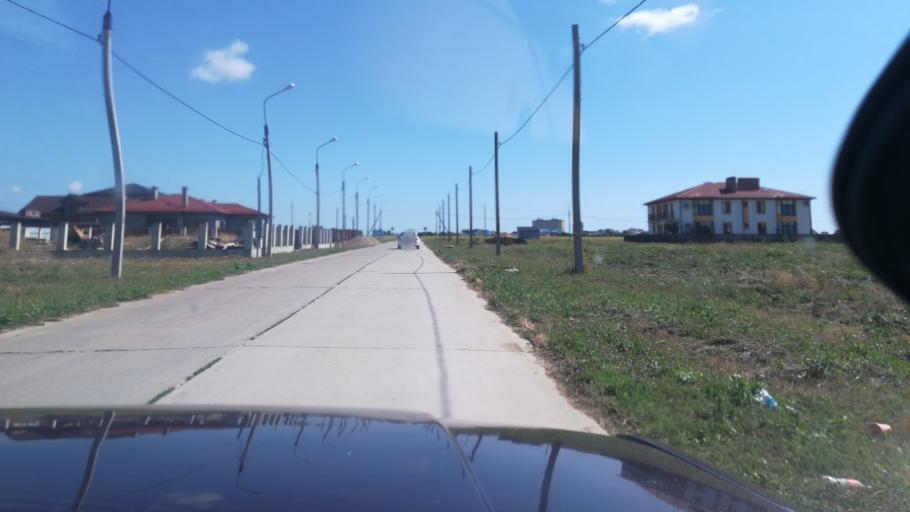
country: RU
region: Krasnodarskiy
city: Vityazevo
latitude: 44.9900
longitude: 37.2756
